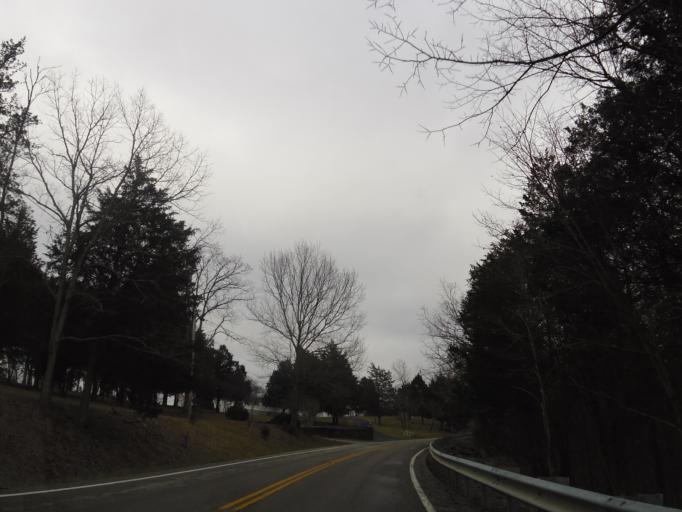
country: US
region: Kentucky
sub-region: Franklin County
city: Frankfort
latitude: 38.3401
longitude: -84.9932
